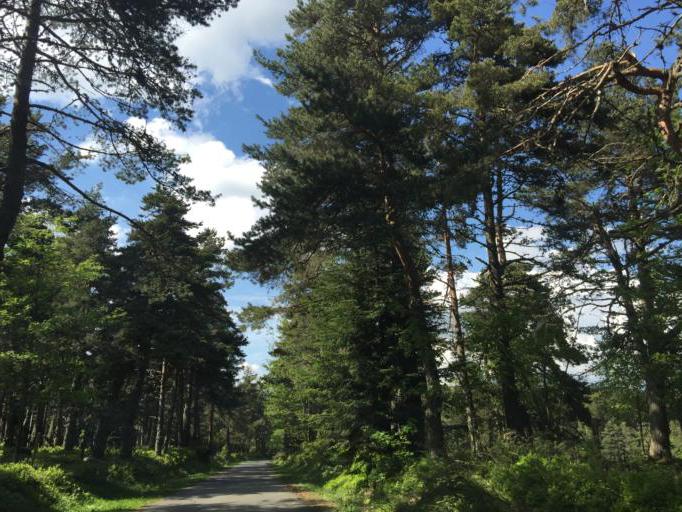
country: FR
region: Rhone-Alpes
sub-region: Departement de la Loire
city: Saint-Sauveur-en-Rue
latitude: 45.2965
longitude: 4.4811
